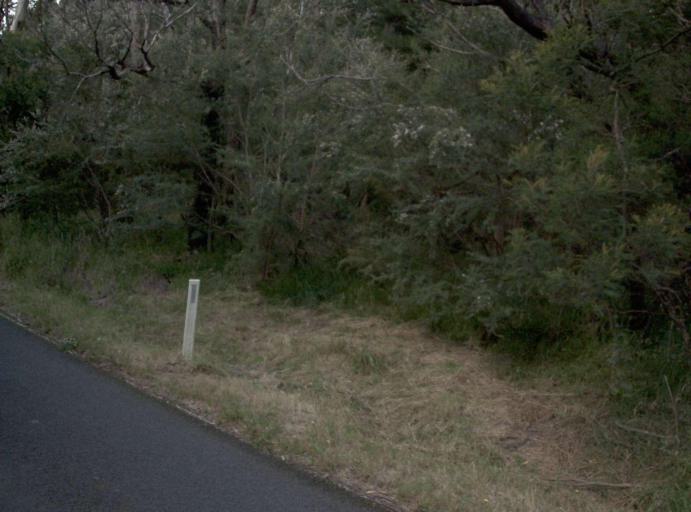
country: AU
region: Victoria
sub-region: Latrobe
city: Morwell
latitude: -38.1955
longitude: 146.4029
